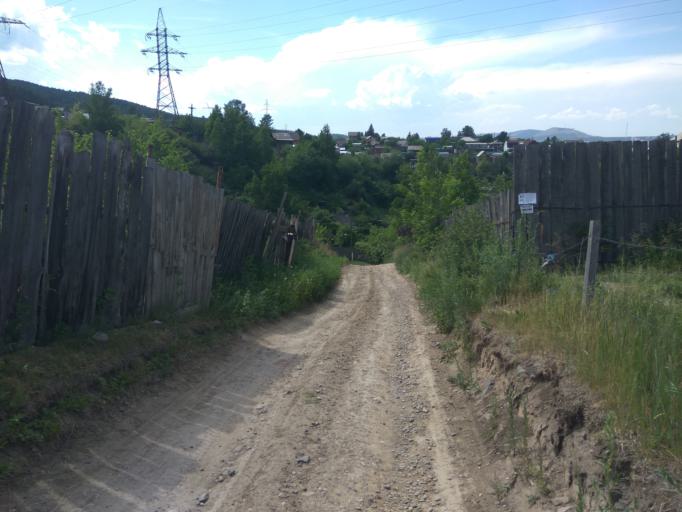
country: RU
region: Krasnoyarskiy
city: Krasnoyarsk
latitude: 55.9678
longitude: 92.8612
